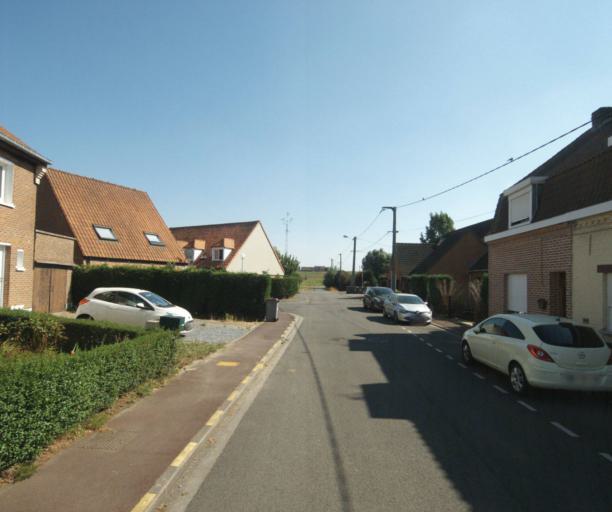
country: FR
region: Nord-Pas-de-Calais
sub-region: Departement du Nord
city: Bousbecque
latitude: 50.7685
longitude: 3.0694
